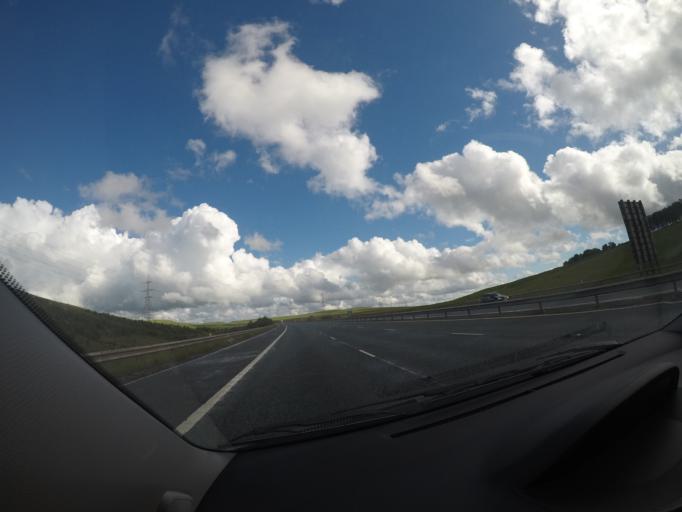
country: GB
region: Scotland
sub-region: South Lanarkshire
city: Douglas
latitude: 55.5483
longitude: -3.7990
